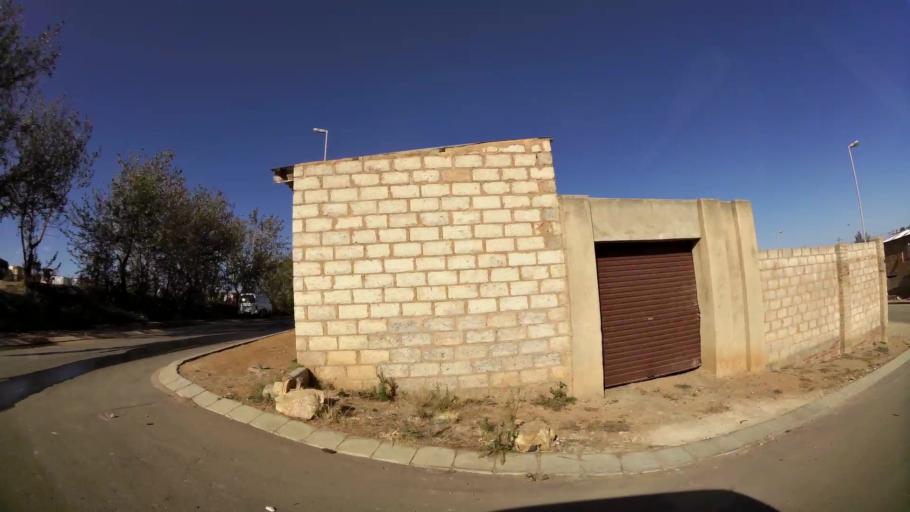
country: ZA
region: Gauteng
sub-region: Ekurhuleni Metropolitan Municipality
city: Tembisa
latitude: -26.0304
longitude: 28.2118
